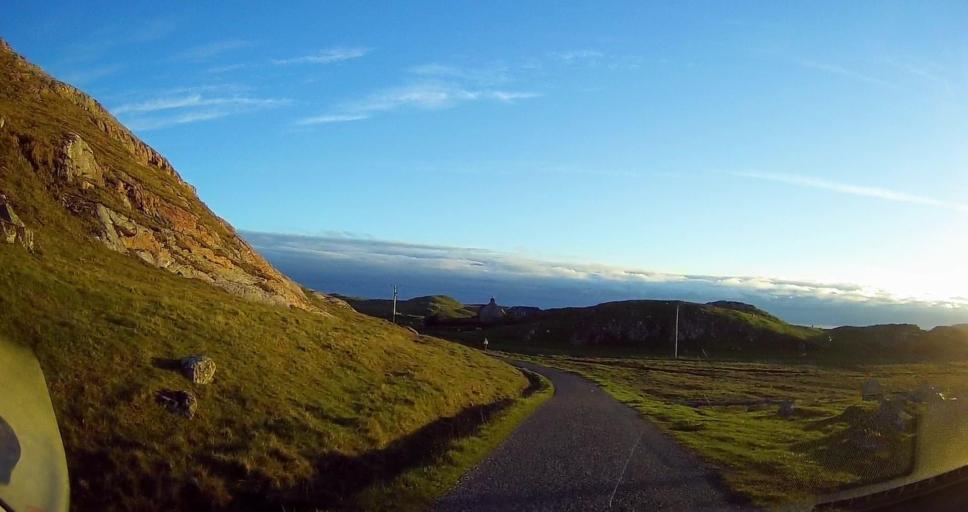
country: GB
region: Scotland
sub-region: Shetland Islands
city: Lerwick
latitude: 60.4438
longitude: -1.4434
